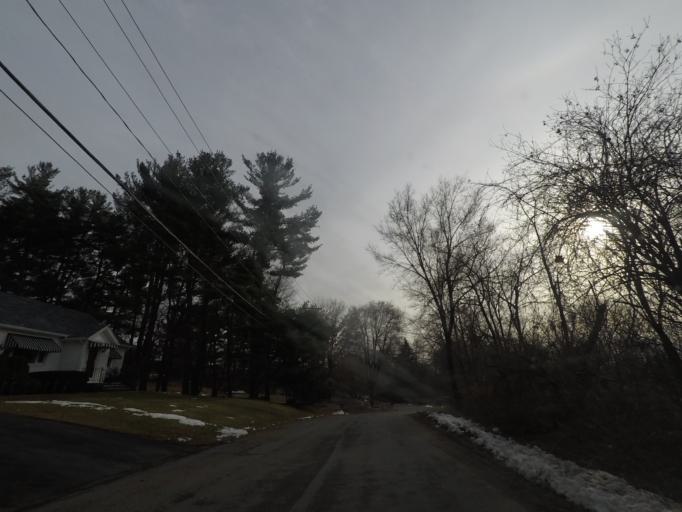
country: US
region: New York
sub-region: Rensselaer County
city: Hampton Manor
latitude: 42.6516
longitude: -73.6870
